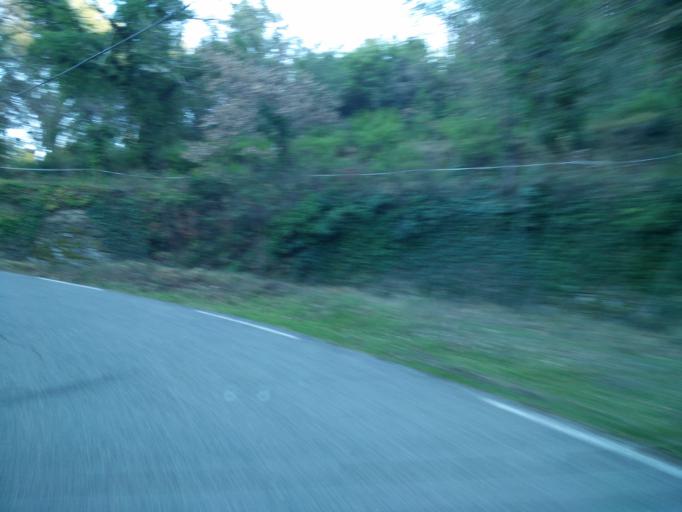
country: FR
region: Provence-Alpes-Cote d'Azur
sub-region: Departement du Var
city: Collobrieres
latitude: 43.2223
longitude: 6.2952
